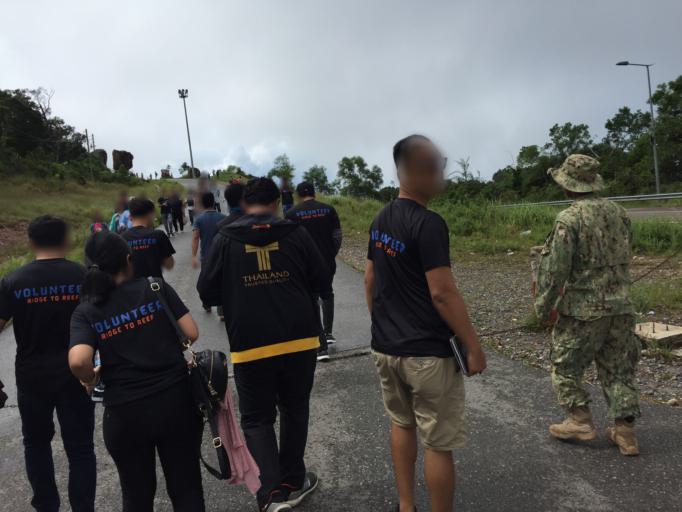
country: KH
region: Kampot
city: Kampot
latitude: 10.6218
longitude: 104.0753
